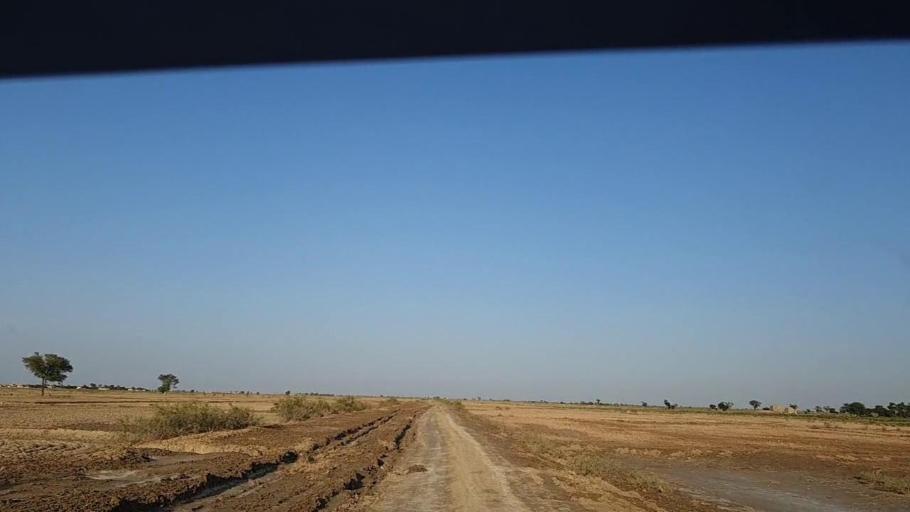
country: PK
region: Sindh
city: Johi
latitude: 26.7443
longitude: 67.6150
